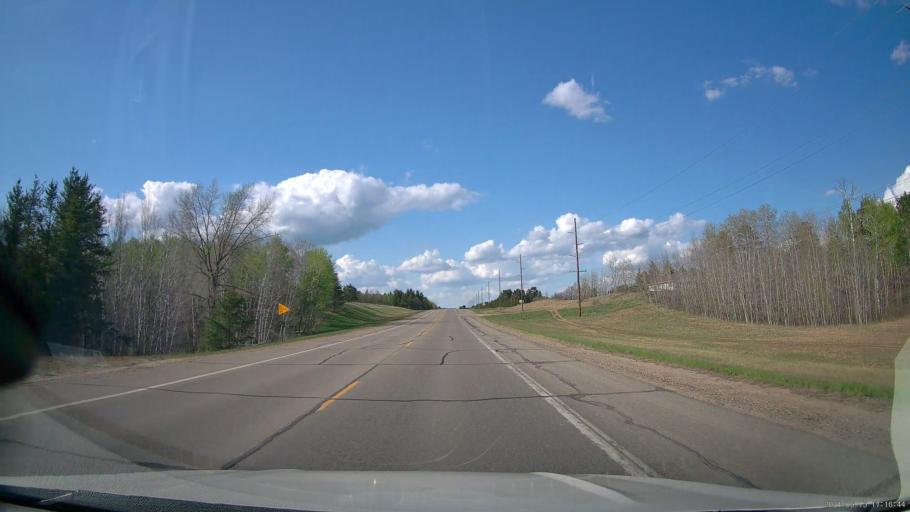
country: US
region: Minnesota
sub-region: Hubbard County
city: Park Rapids
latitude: 46.9333
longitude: -95.0168
